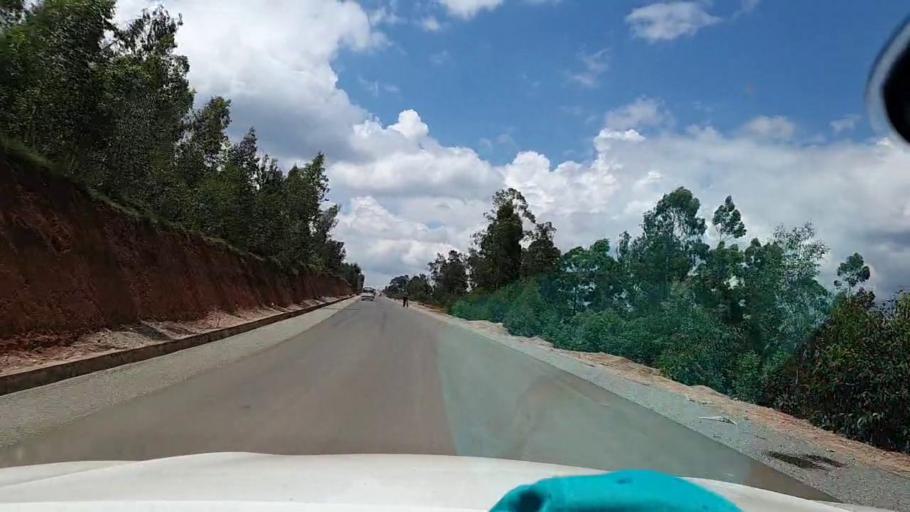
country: RW
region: Southern Province
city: Nzega
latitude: -2.6414
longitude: 29.5773
